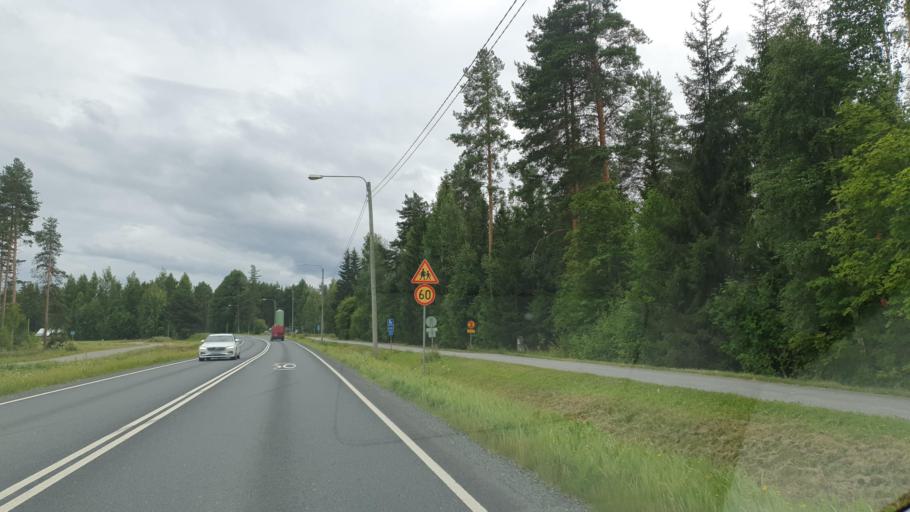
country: FI
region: Northern Savo
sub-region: Ylae-Savo
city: Lapinlahti
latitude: 63.4233
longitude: 27.3303
